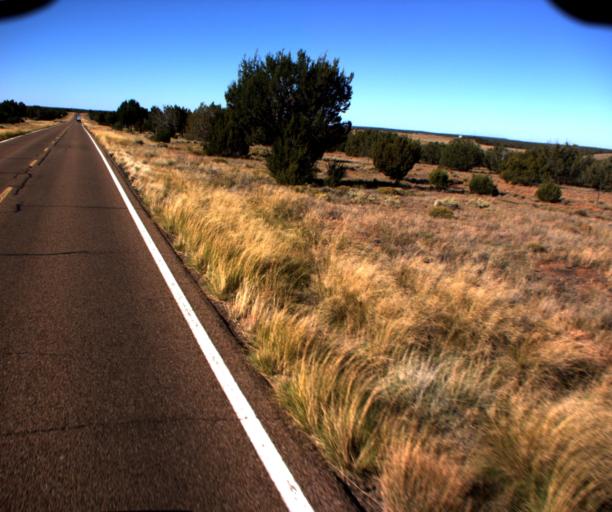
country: US
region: Arizona
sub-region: Navajo County
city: Heber-Overgaard
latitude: 34.5156
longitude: -110.4390
